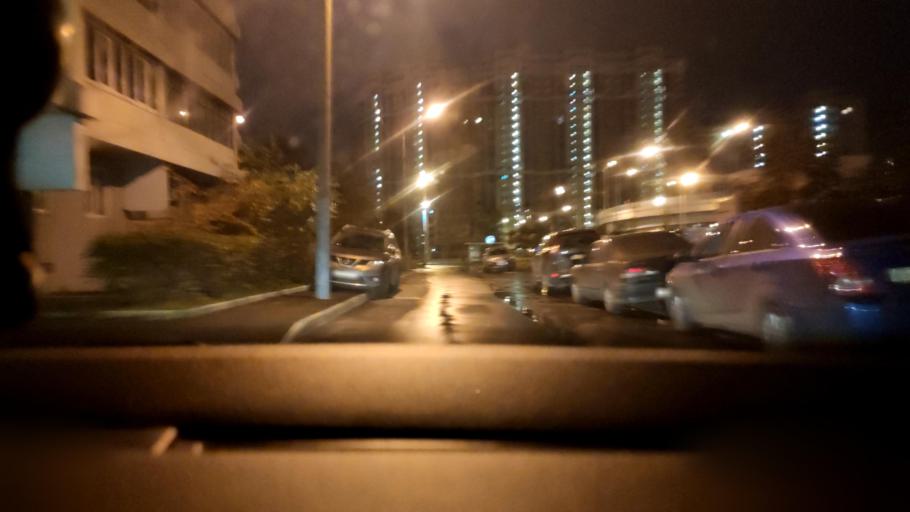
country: RU
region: Moskovskaya
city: Bol'shaya Setun'
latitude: 55.7399
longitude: 37.4357
